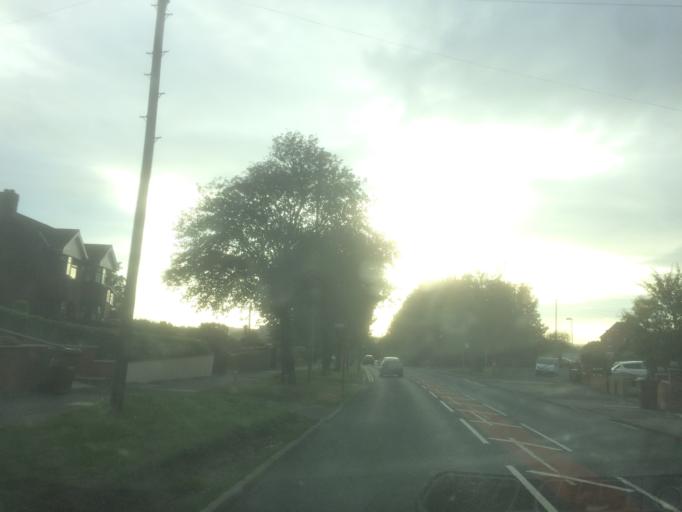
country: GB
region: England
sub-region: City and Borough of Wakefield
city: Pontefract
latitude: 53.7161
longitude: -1.3298
